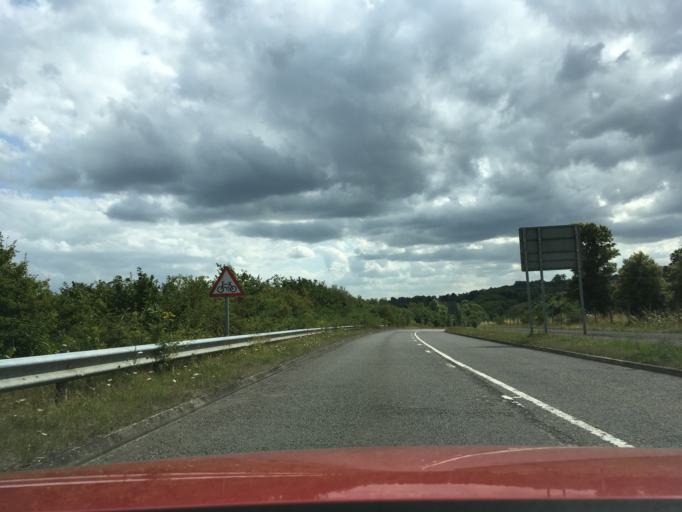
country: GB
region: England
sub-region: West Berkshire
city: Winterbourne
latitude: 51.4375
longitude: -1.3220
